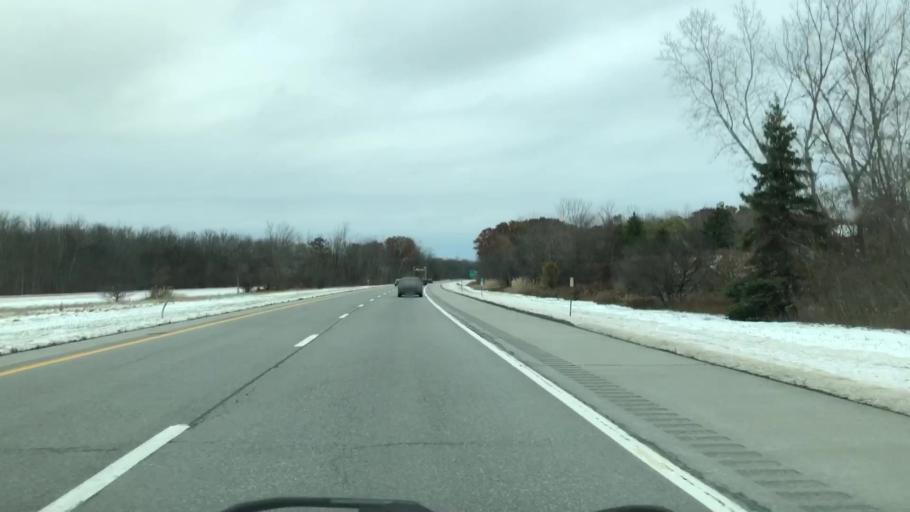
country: US
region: New York
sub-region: Monroe County
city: Spencerport
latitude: 43.1139
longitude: -77.7720
